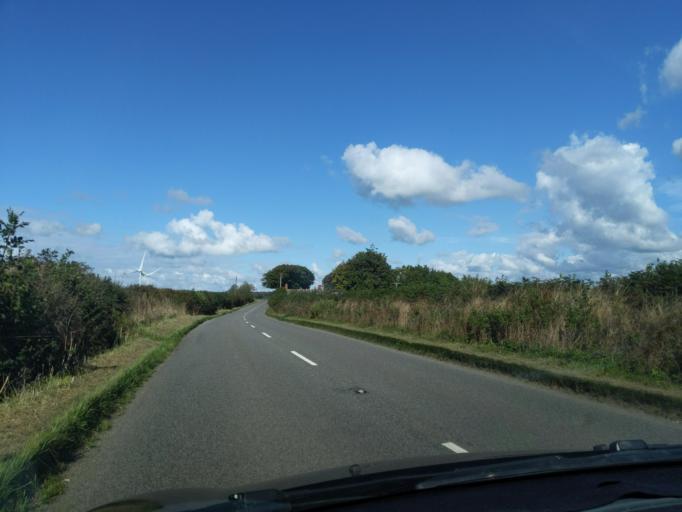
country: GB
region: England
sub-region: Cornwall
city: Boyton
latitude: 50.7356
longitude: -4.3239
